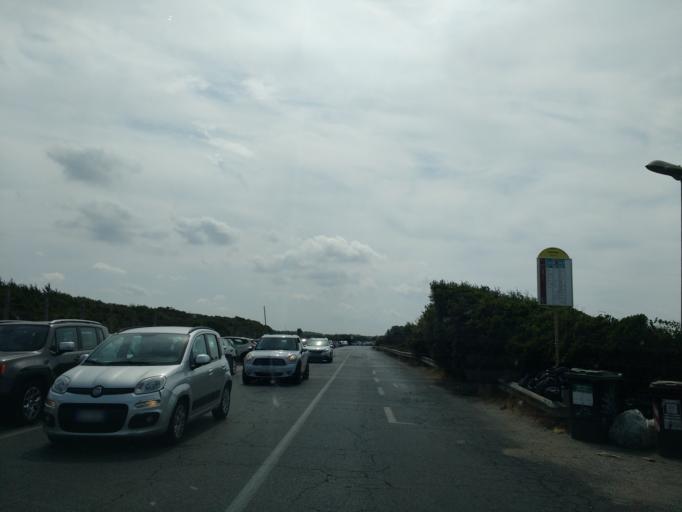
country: IT
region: Latium
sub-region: Citta metropolitana di Roma Capitale
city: Torvaianica
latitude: 41.6715
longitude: 12.3965
